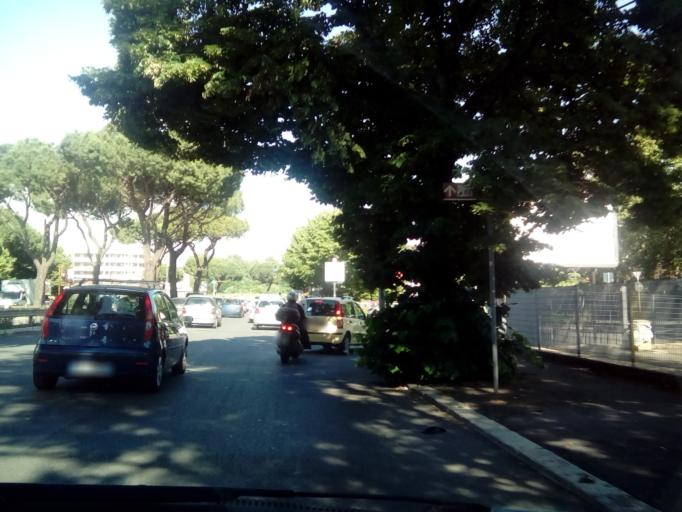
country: IT
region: Latium
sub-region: Citta metropolitana di Roma Capitale
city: Rome
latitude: 41.8949
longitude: 12.5732
